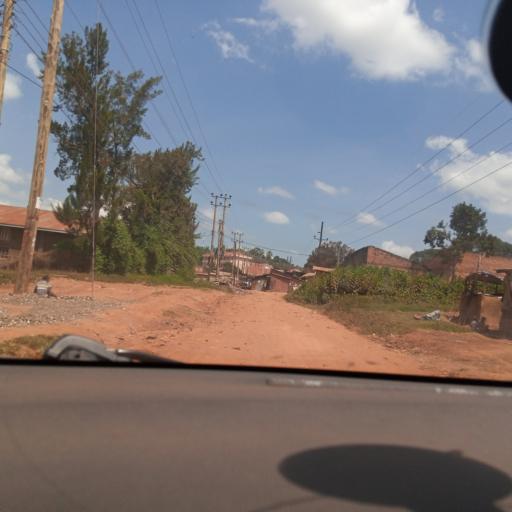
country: UG
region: Central Region
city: Masaka
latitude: -0.3309
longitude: 31.7427
